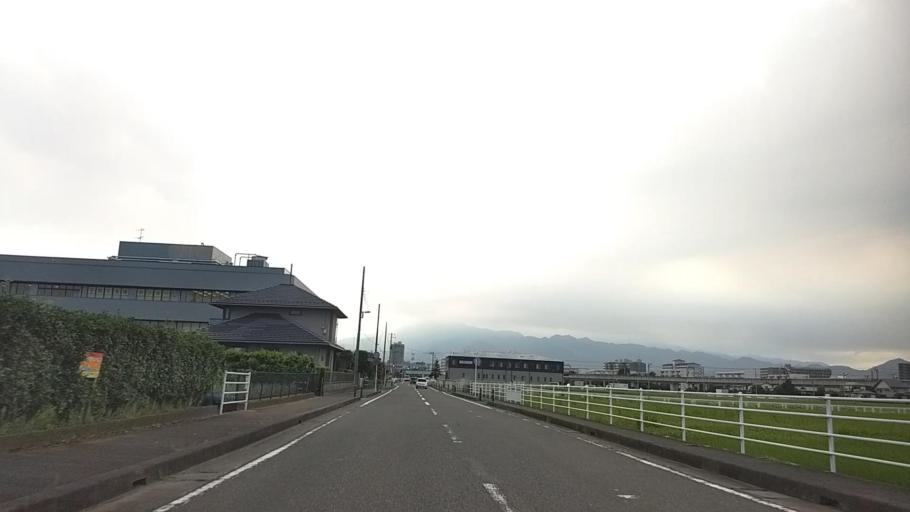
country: JP
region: Kanagawa
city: Atsugi
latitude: 35.4449
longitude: 139.3874
